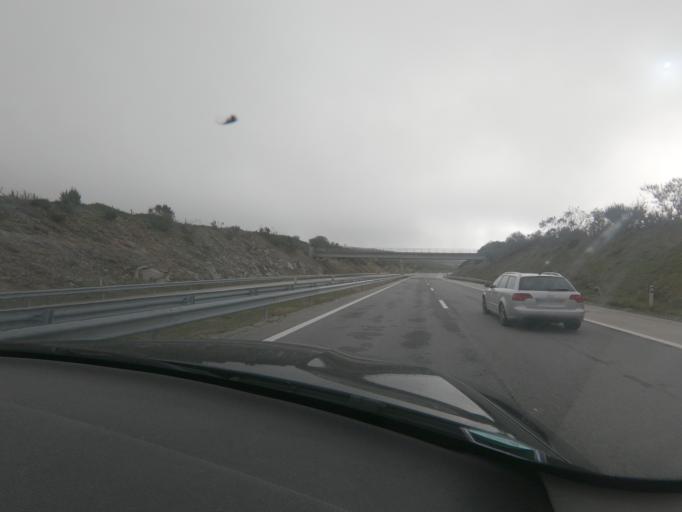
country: PT
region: Viseu
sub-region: Tarouca
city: Tarouca
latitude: 40.9978
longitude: -7.8824
